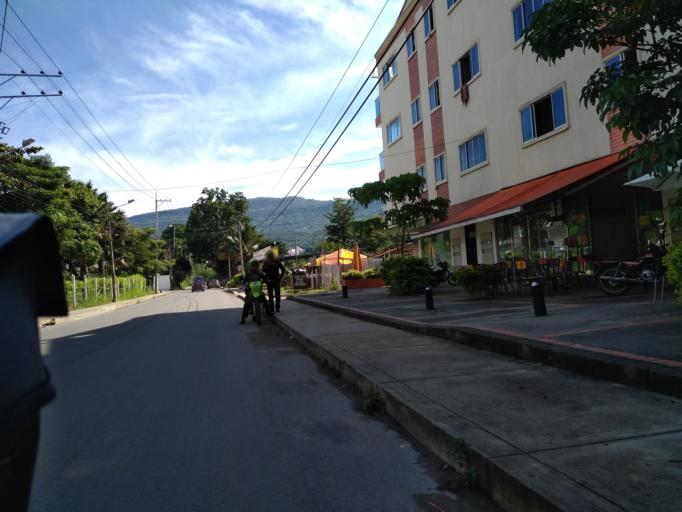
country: CO
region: Santander
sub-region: San Gil
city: San Gil
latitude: 6.5397
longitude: -73.1272
